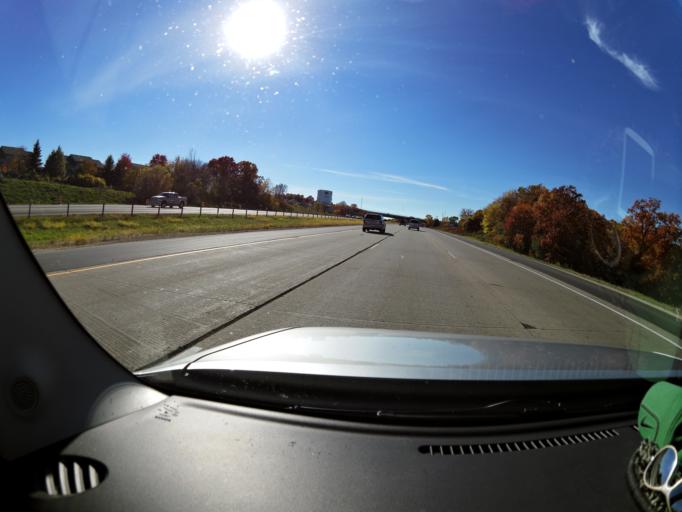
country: US
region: Minnesota
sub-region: Dakota County
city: Eagan
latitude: 44.8134
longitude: -93.1792
